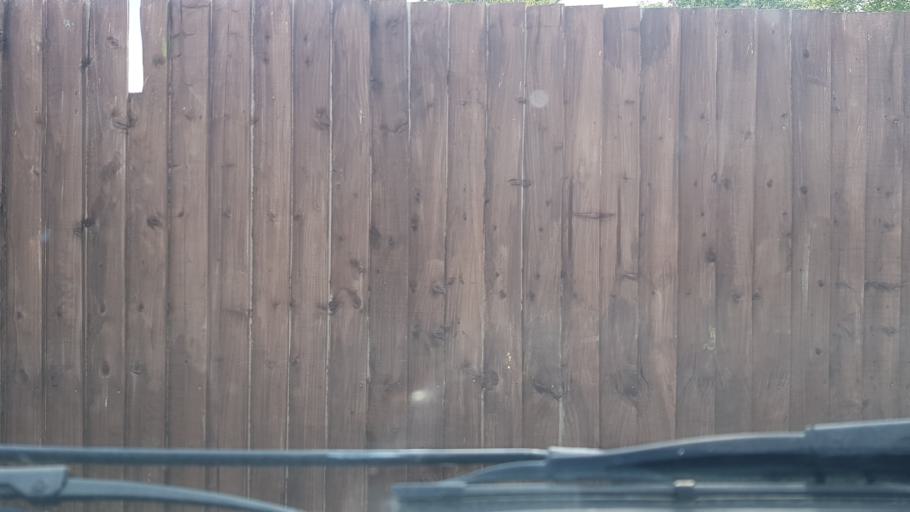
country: GB
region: England
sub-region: Worcestershire
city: Stourport-on-Severn
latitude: 52.3422
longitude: -2.2767
